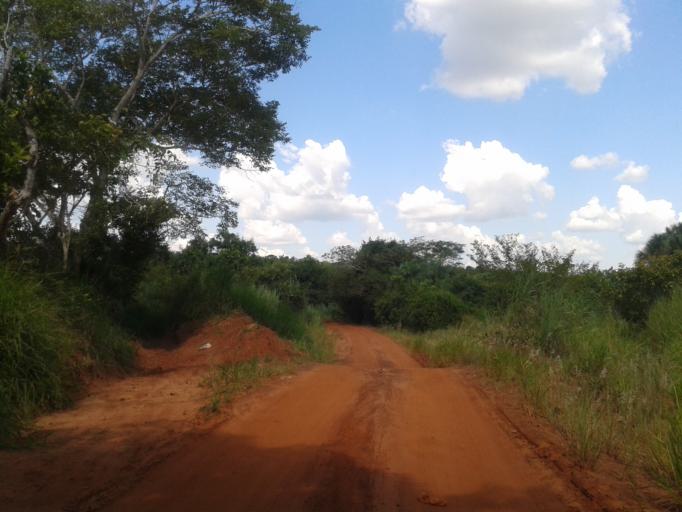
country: BR
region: Minas Gerais
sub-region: Ituiutaba
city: Ituiutaba
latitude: -19.1826
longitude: -49.7312
